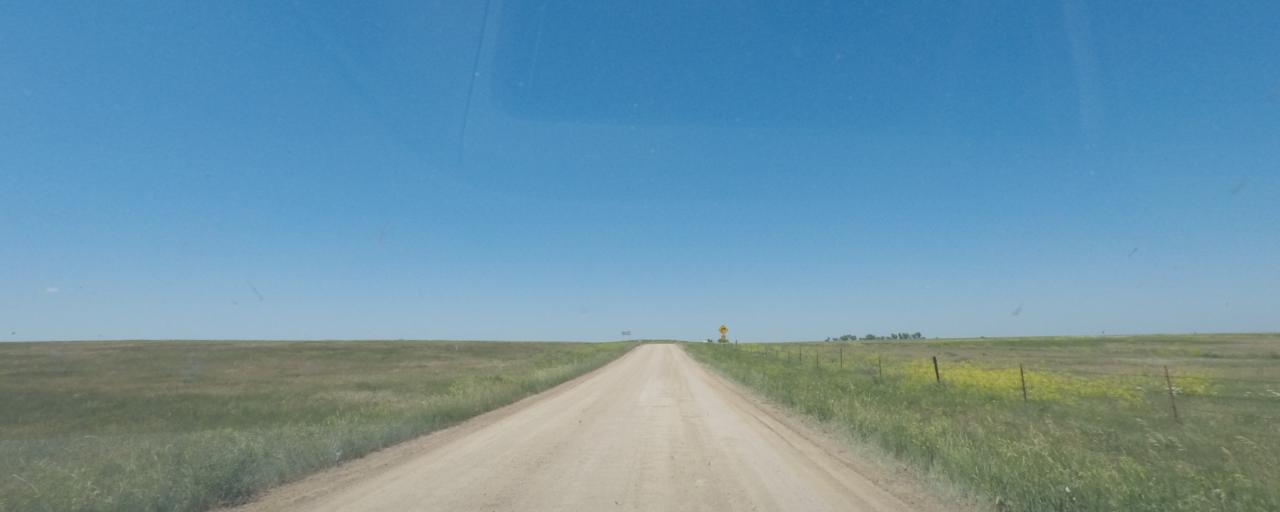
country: US
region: South Dakota
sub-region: Haakon County
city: Philip
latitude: 43.9343
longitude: -102.1587
